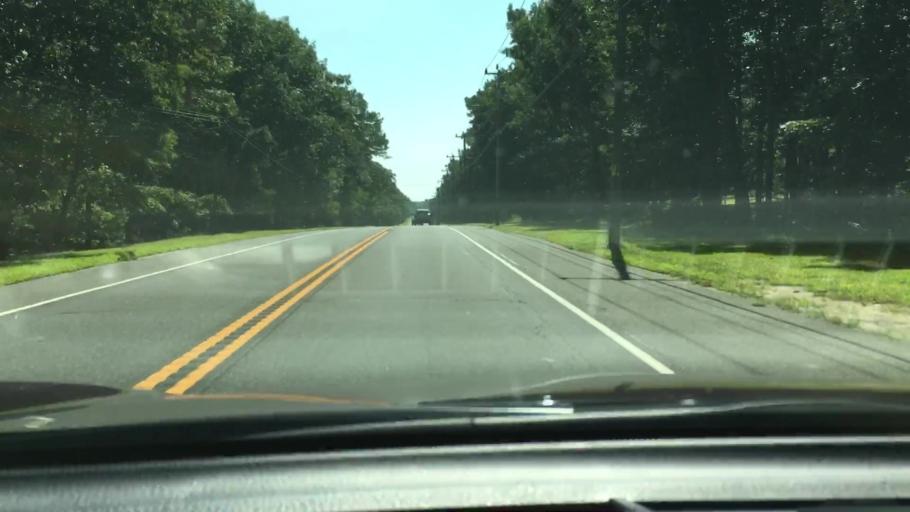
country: US
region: New Jersey
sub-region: Cumberland County
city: Millville
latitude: 39.3810
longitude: -74.9709
